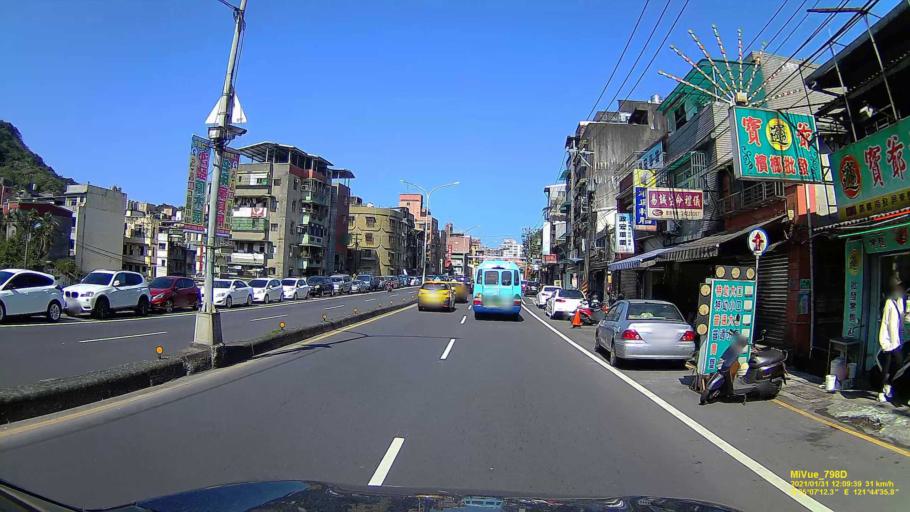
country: TW
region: Taiwan
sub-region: Keelung
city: Keelung
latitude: 25.1203
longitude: 121.7432
